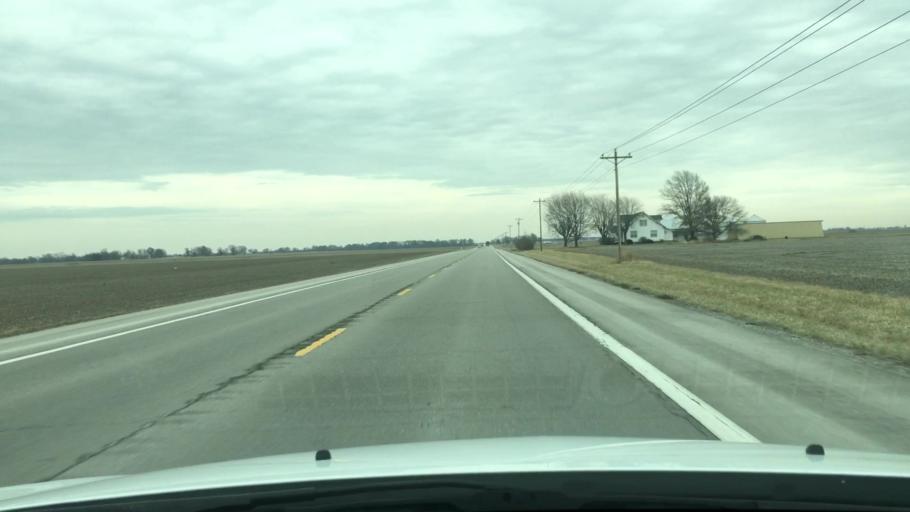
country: US
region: Missouri
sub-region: Audrain County
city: Mexico
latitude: 39.1639
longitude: -91.7808
